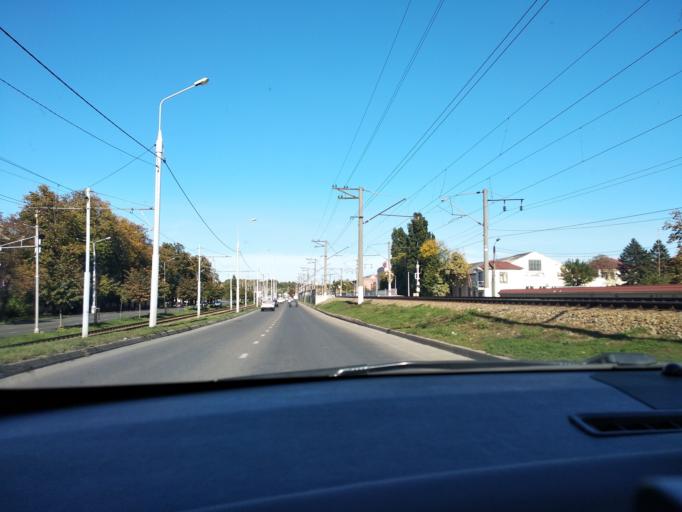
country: RU
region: Adygeya
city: Yablonovskiy
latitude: 45.0036
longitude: 38.9656
